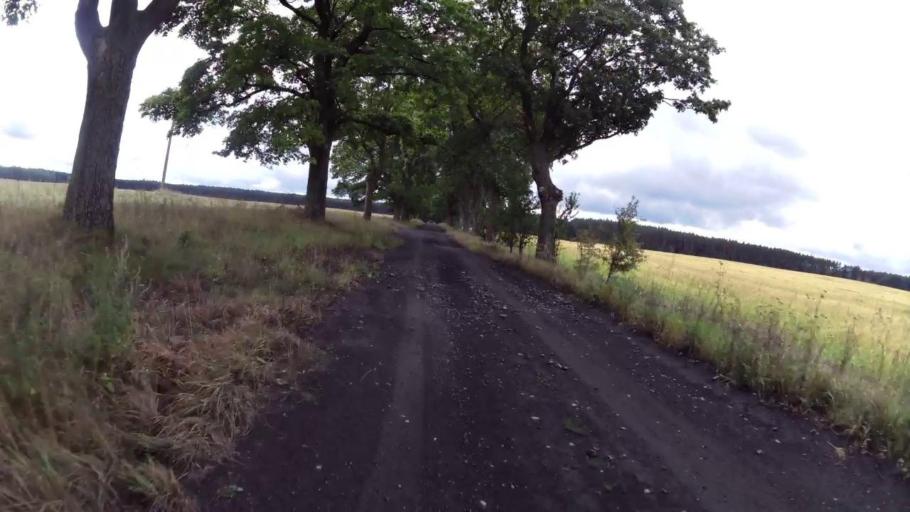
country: PL
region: West Pomeranian Voivodeship
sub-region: Powiat mysliborski
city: Debno
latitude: 52.8751
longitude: 14.7124
